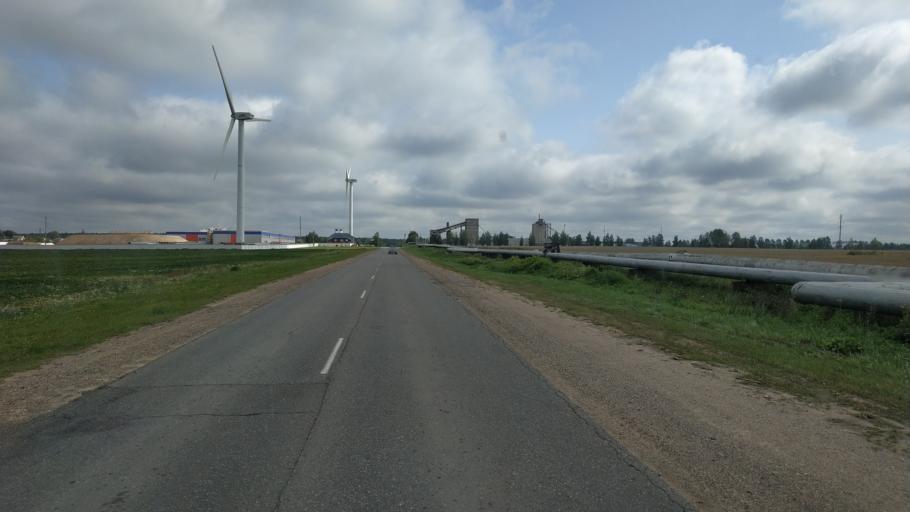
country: BY
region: Mogilev
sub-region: Mahilyowski Rayon
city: Veyno
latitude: 53.8375
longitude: 30.3720
